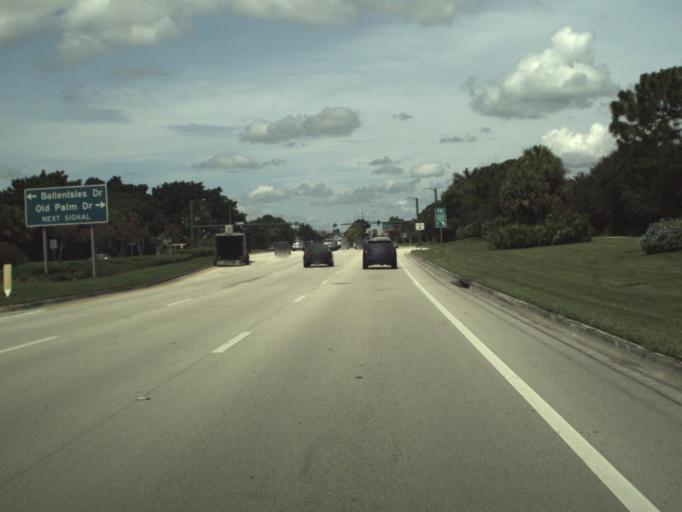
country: US
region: Florida
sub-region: Palm Beach County
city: Palm Beach Gardens
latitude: 26.8389
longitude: -80.1234
